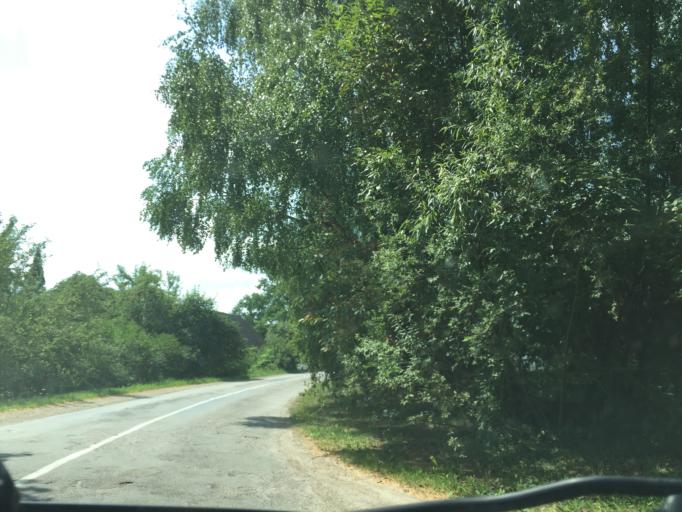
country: LV
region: Tervete
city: Zelmeni
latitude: 56.4050
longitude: 23.3298
